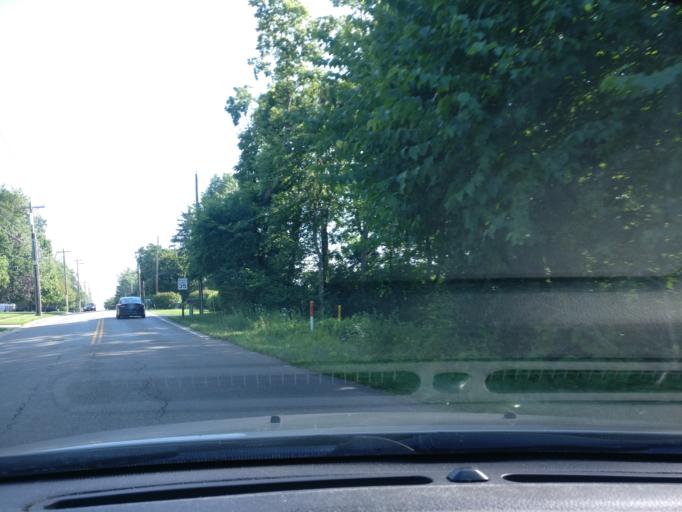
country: US
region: Ohio
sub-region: Warren County
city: Springboro
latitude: 39.5708
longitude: -84.2518
